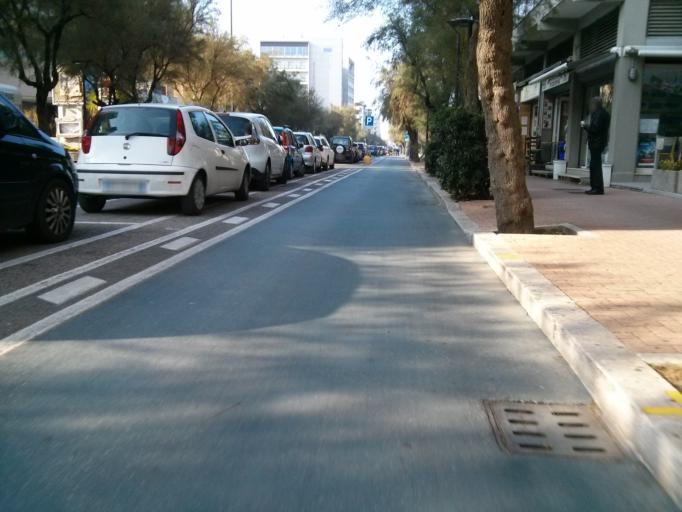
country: IT
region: The Marches
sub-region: Provincia di Pesaro e Urbino
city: Pesaro
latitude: 43.9150
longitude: 12.9163
